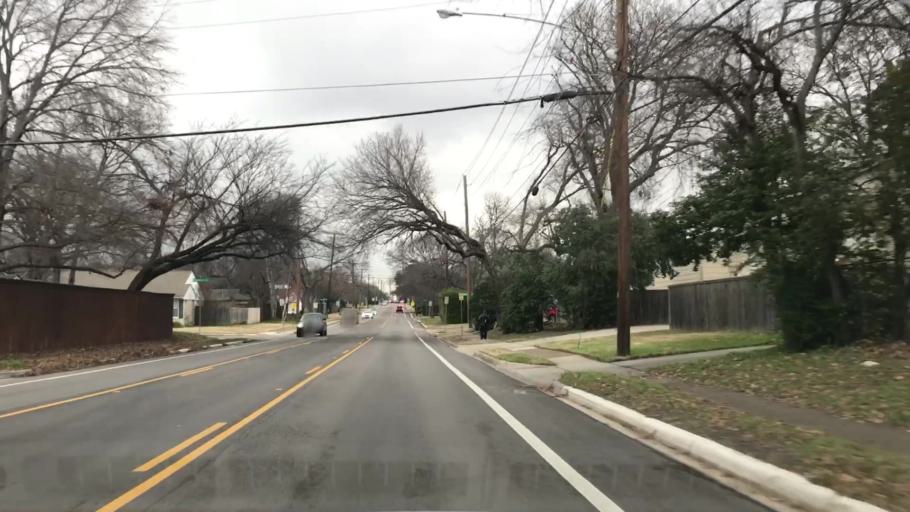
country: US
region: Texas
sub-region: Dallas County
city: Highland Park
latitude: 32.8317
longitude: -96.7679
